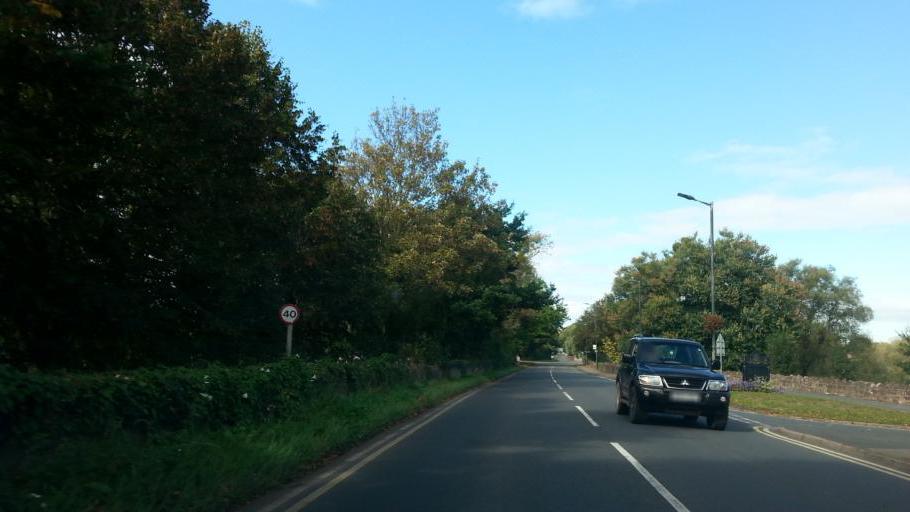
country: GB
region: England
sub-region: Herefordshire
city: Ross on Wye
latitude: 51.9127
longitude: -2.5917
